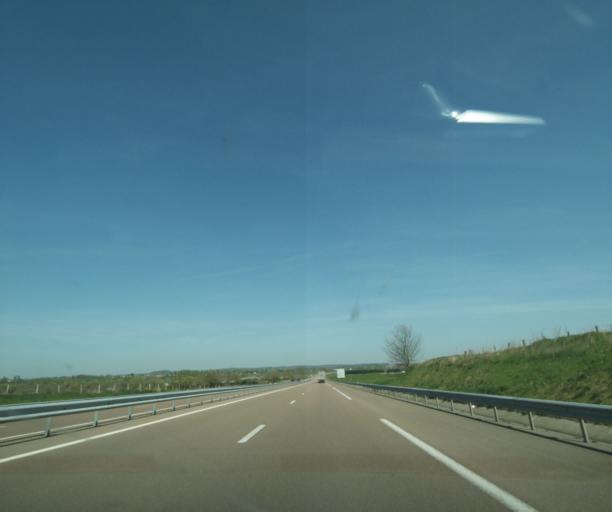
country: FR
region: Bourgogne
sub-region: Departement de la Nievre
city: Magny-Cours
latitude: 46.8605
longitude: 3.1482
